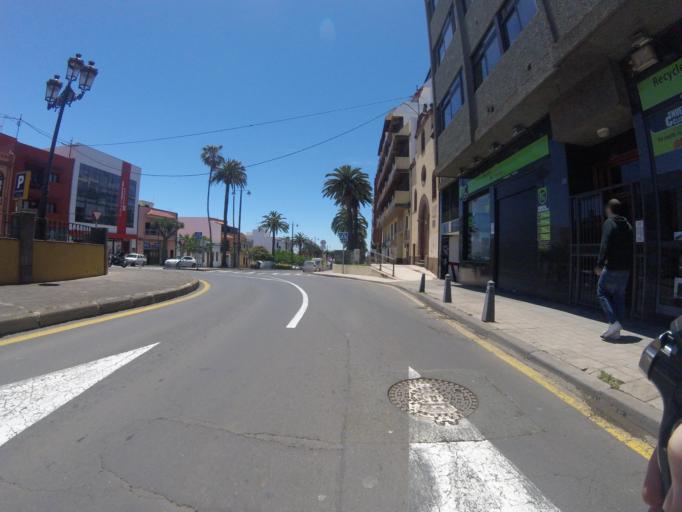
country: ES
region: Canary Islands
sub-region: Provincia de Santa Cruz de Tenerife
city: La Laguna
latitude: 28.4840
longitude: -16.3140
